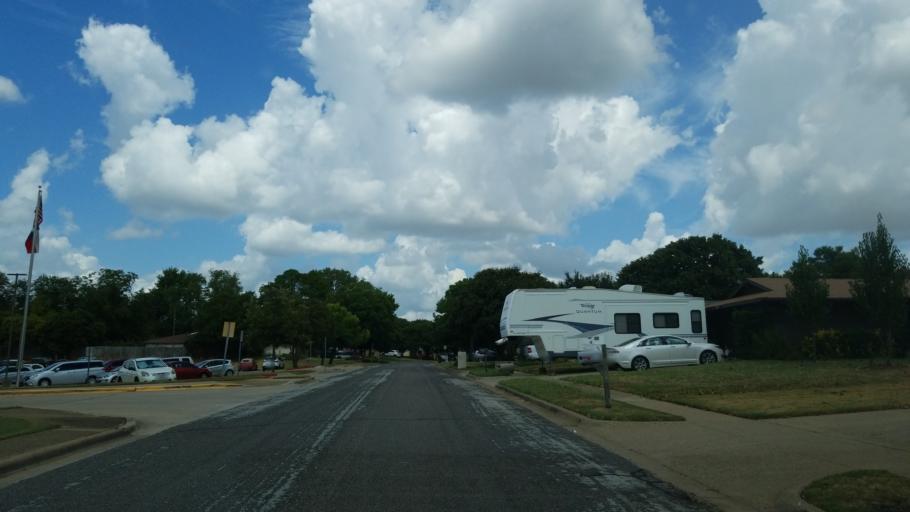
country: US
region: Texas
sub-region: Tarrant County
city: Euless
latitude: 32.8528
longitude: -97.0876
